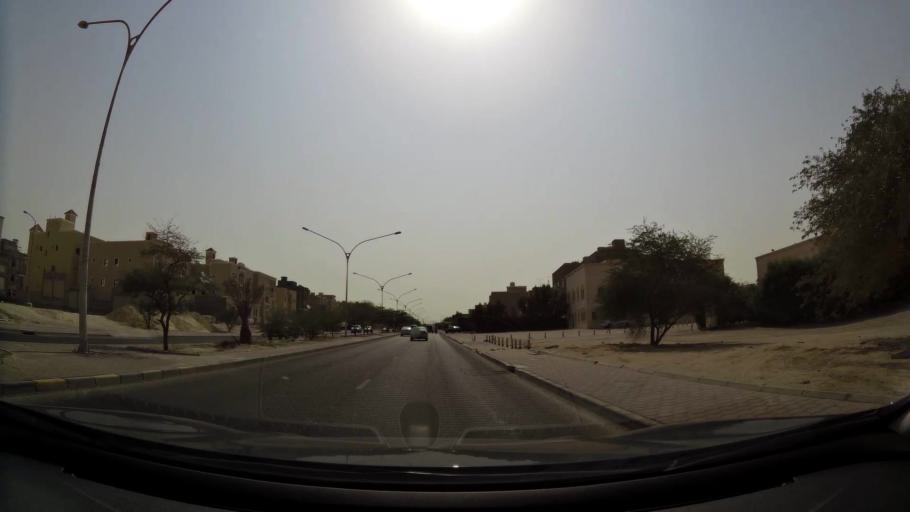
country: KW
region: Muhafazat al Jahra'
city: Al Jahra'
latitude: 29.3238
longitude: 47.6800
